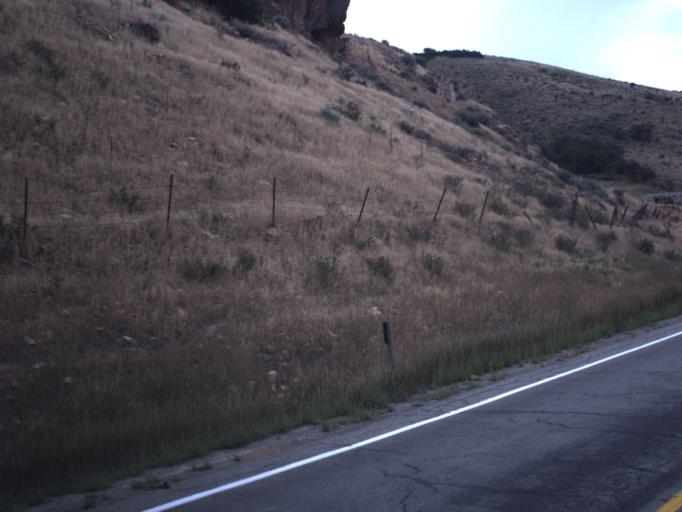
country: US
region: Utah
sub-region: Summit County
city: Oakley
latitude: 40.7320
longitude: -111.3476
